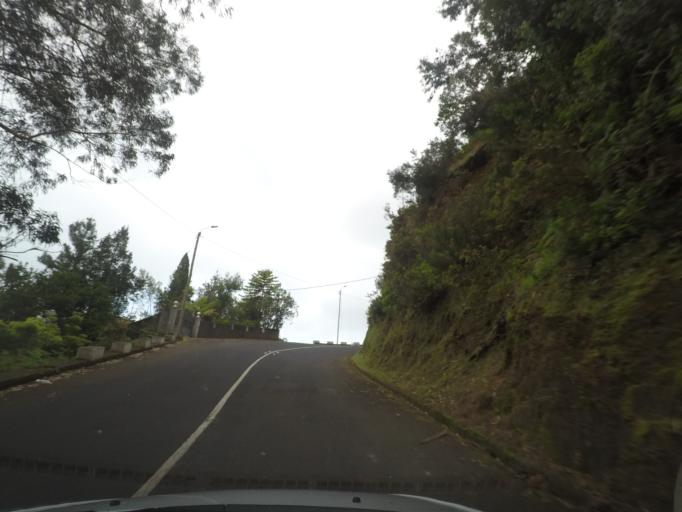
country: PT
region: Madeira
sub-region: Santana
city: Santana
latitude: 32.7515
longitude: -16.8372
